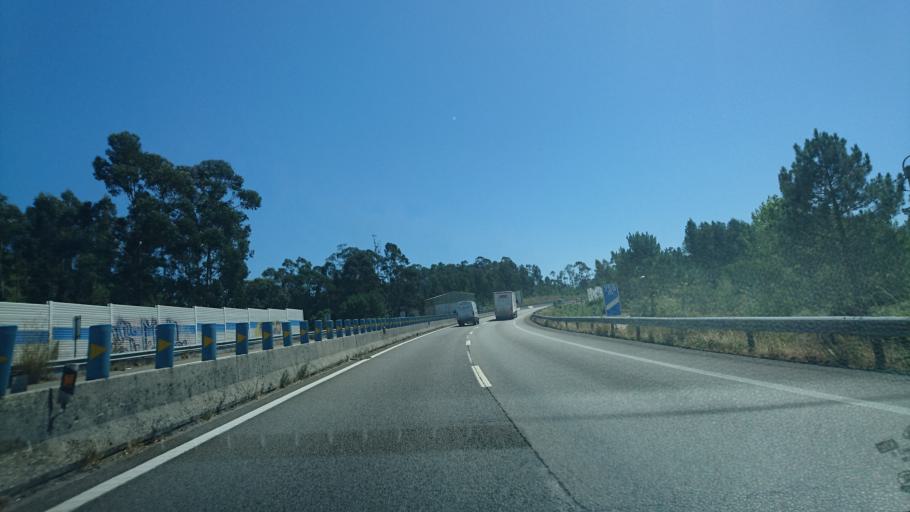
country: PT
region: Porto
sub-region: Vila Nova de Gaia
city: Sao Felix da Marinha
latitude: 41.0311
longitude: -8.6244
